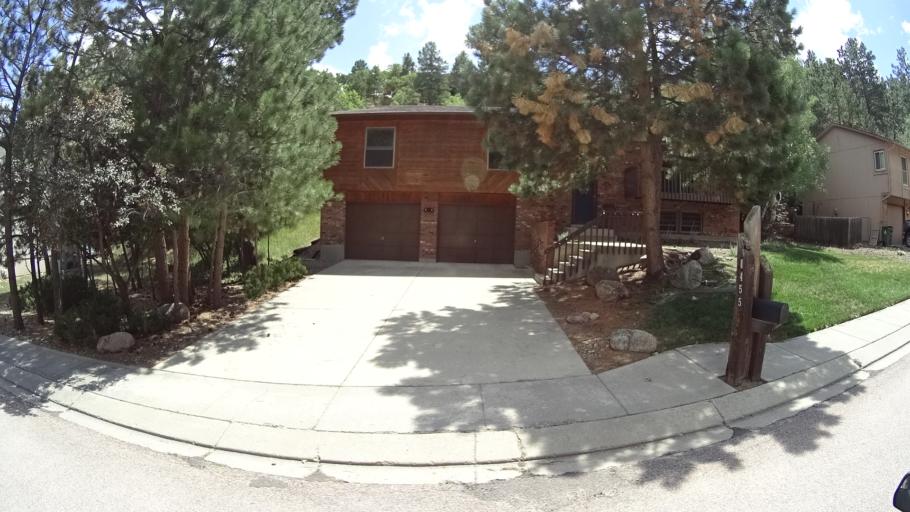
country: US
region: Colorado
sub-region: El Paso County
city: Air Force Academy
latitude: 38.9397
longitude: -104.8563
